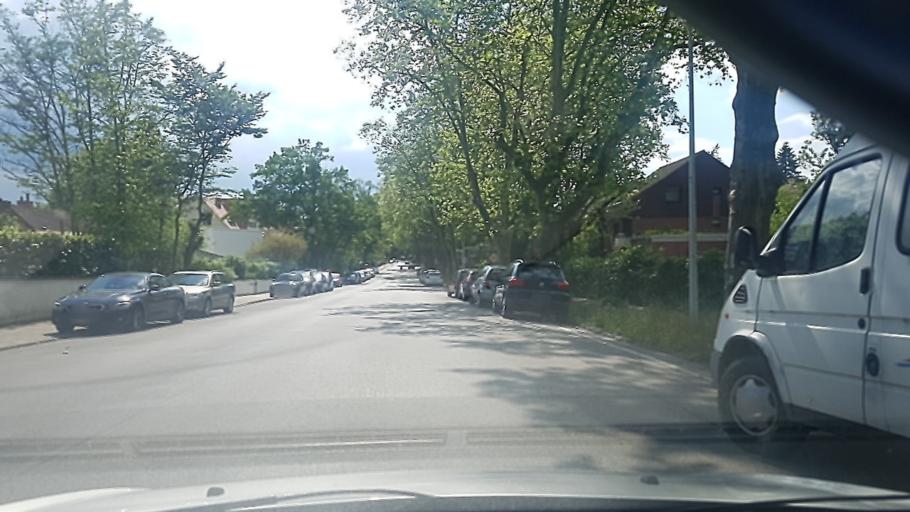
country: DE
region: Hesse
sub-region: Regierungsbezirk Darmstadt
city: Darmstadt
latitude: 49.8826
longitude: 8.6813
